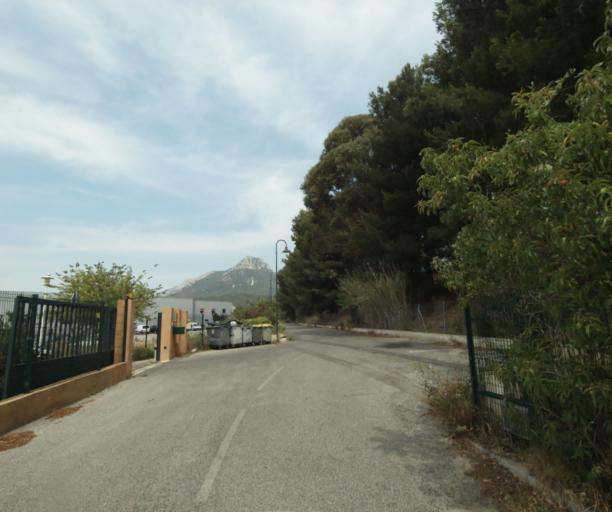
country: FR
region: Provence-Alpes-Cote d'Azur
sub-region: Departement du Var
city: La Farlede
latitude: 43.1385
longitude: 6.0399
